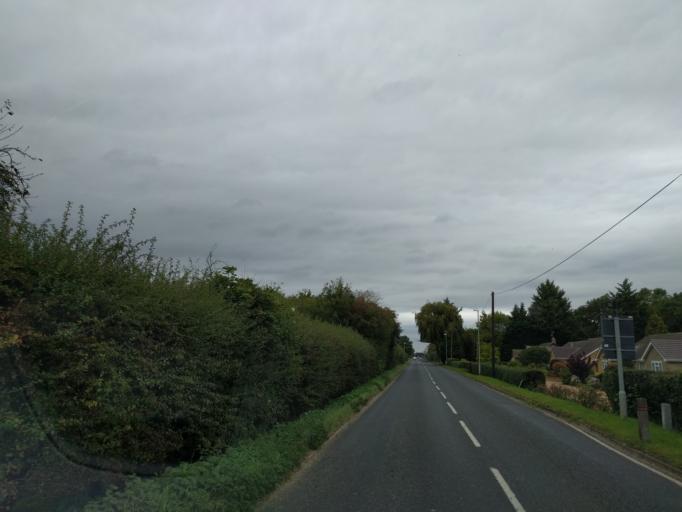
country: GB
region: England
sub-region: Cambridgeshire
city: Earith
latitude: 52.3197
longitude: 0.0599
